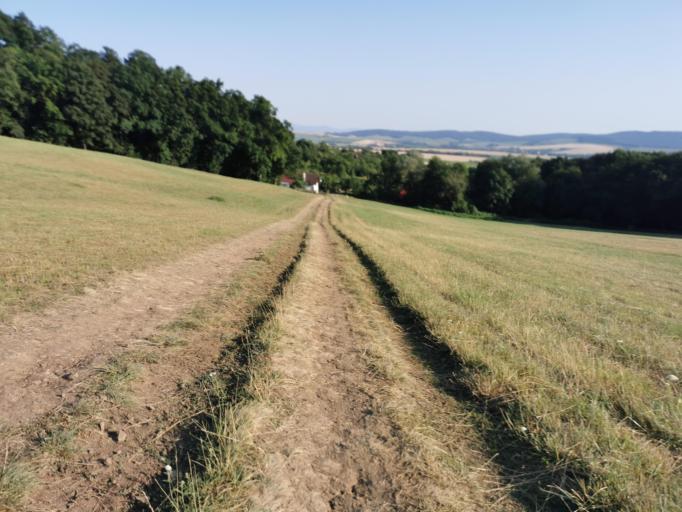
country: CZ
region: South Moravian
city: Sudomerice
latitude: 48.8065
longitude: 17.2920
